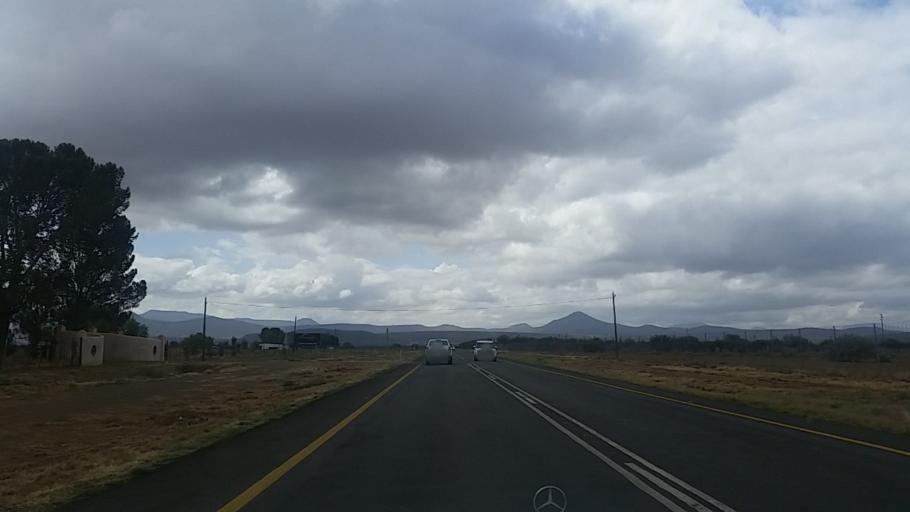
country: ZA
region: Eastern Cape
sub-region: Cacadu District Municipality
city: Graaff-Reinet
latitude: -32.1928
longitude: 24.5564
